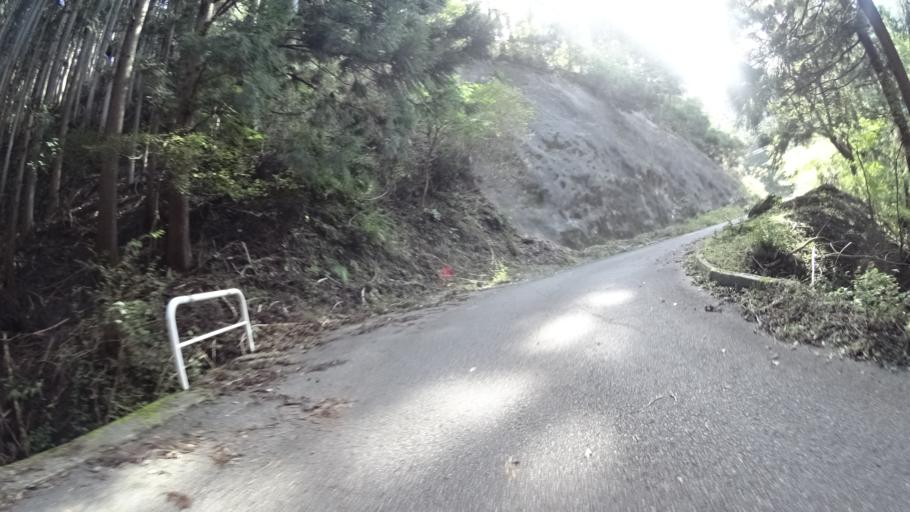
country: JP
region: Yamanashi
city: Otsuki
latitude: 35.5783
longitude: 138.9815
